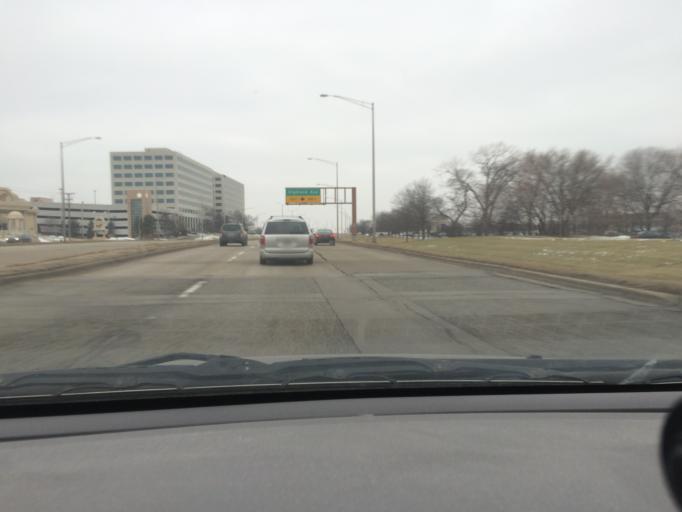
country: US
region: Illinois
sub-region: DuPage County
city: Downers Grove
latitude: 41.8375
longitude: -88.0045
